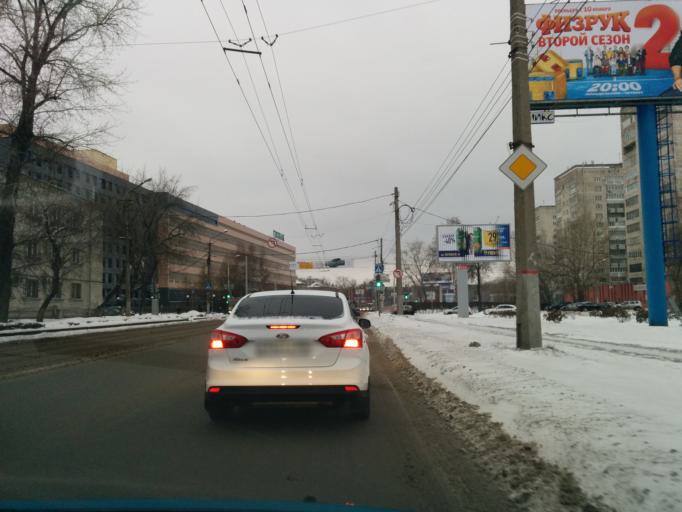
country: RU
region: Perm
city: Perm
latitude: 57.9917
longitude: 56.2003
